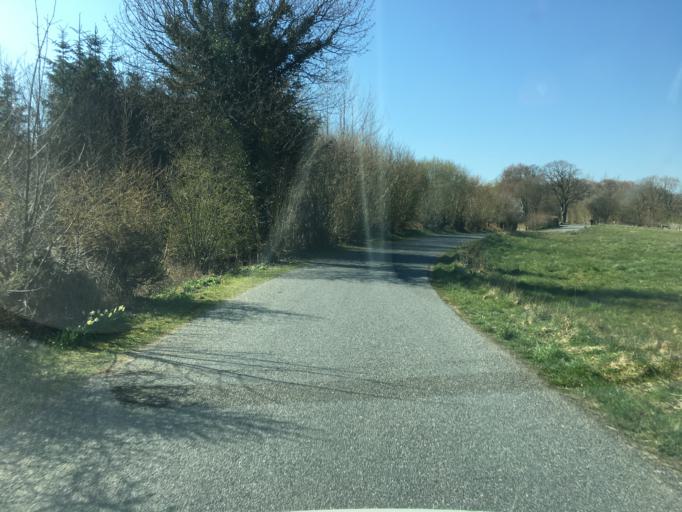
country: DK
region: South Denmark
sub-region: Aabenraa Kommune
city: Krusa
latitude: 54.9254
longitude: 9.4429
